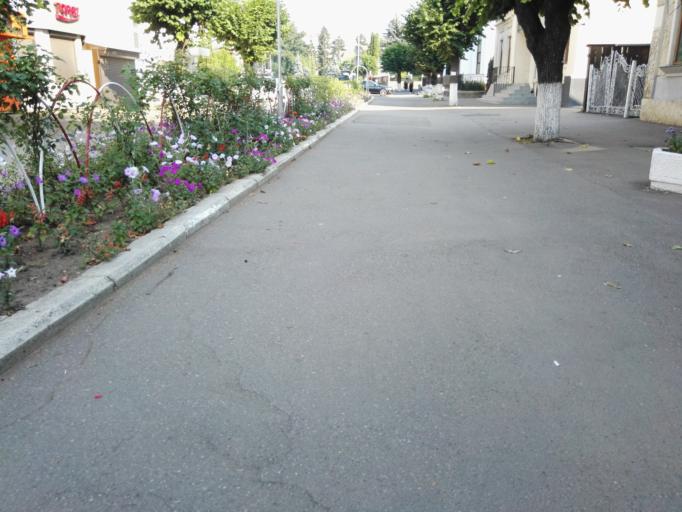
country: RO
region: Suceava
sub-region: Municipiul Falticeni
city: Falticeni
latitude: 47.4632
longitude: 26.2991
